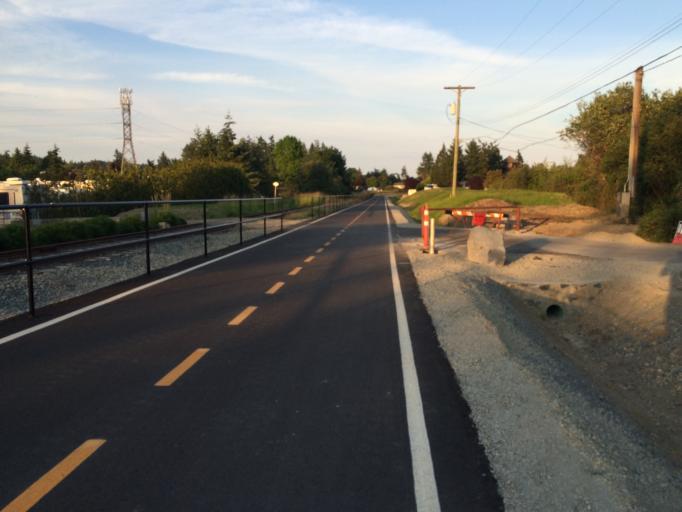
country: CA
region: British Columbia
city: Colwood
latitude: 48.4604
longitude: -123.4473
